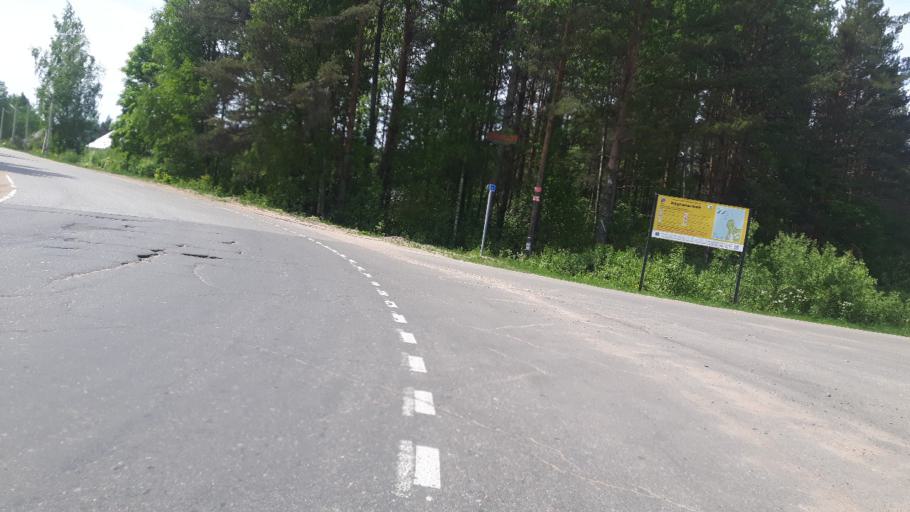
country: RU
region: Leningrad
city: Ust'-Luga
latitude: 59.6578
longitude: 28.2493
